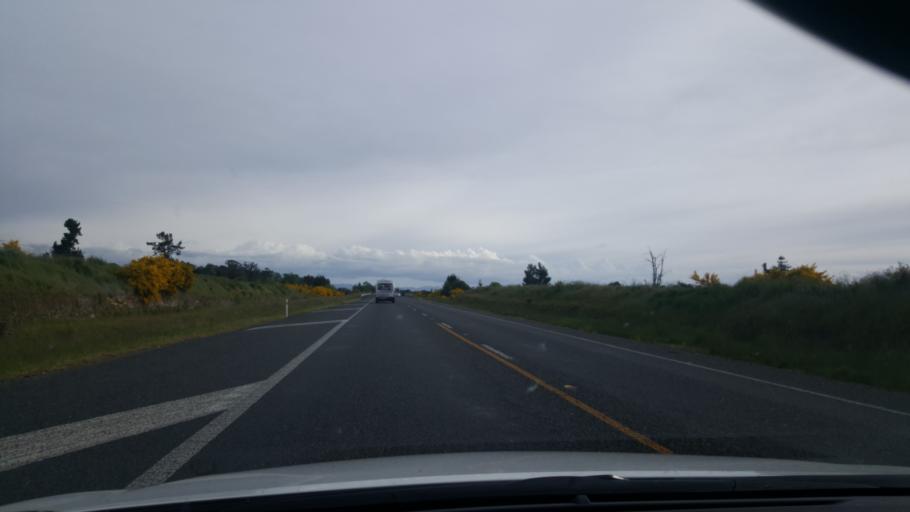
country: NZ
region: Waikato
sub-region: Taupo District
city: Taupo
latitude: -38.6521
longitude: 176.1003
